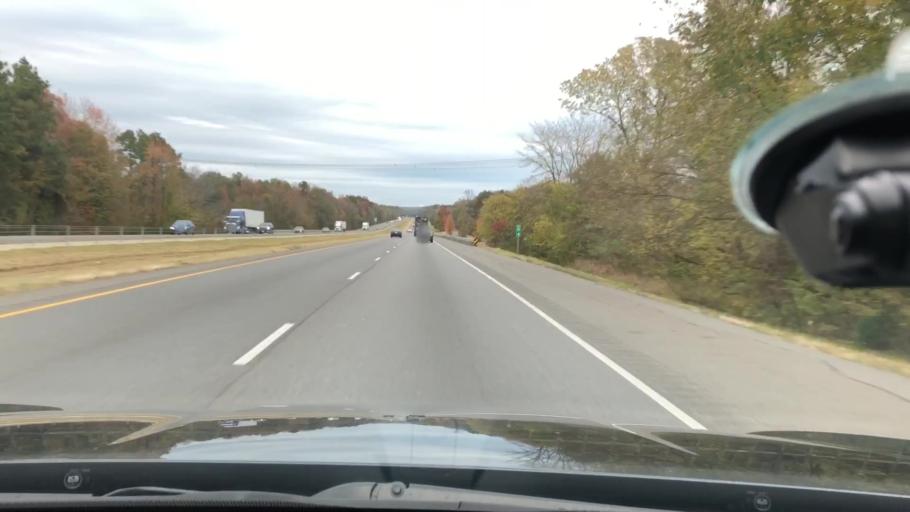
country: US
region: Arkansas
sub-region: Hot Spring County
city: Malvern
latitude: 34.3574
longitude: -92.8811
